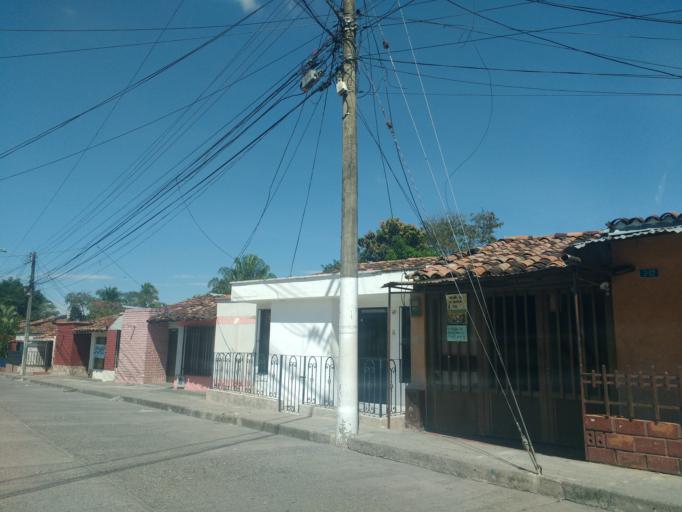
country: CO
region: Valle del Cauca
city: Cartago
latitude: 4.7517
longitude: -75.8994
